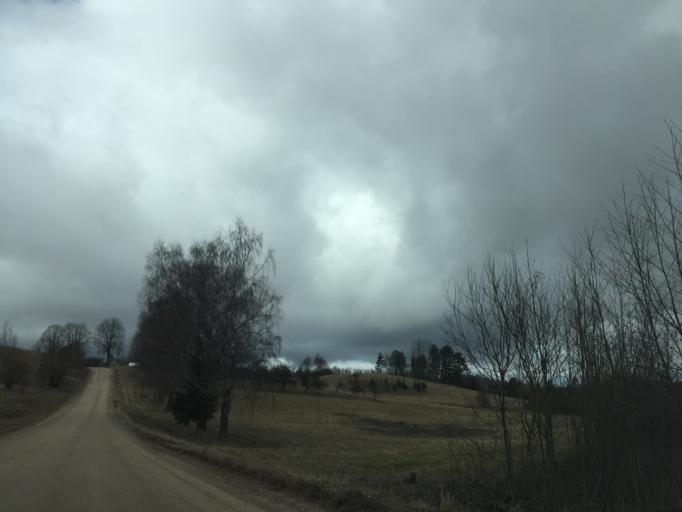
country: LV
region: Ilukste
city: Ilukste
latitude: 56.0666
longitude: 26.0916
